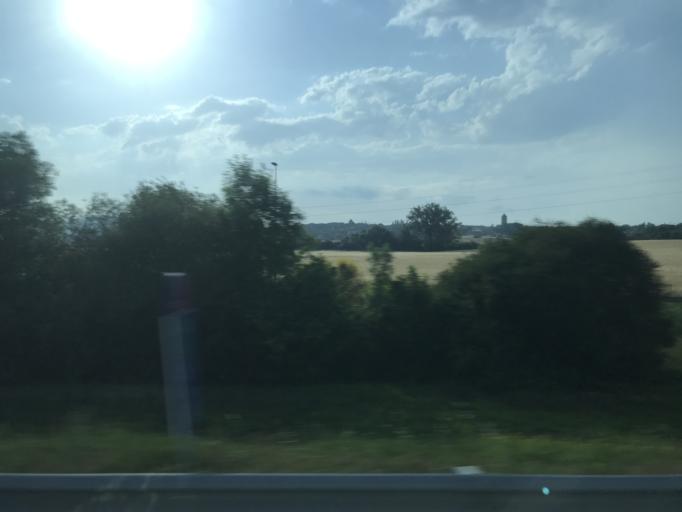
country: ES
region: Basque Country
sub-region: Provincia de Alava
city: Gasteiz / Vitoria
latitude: 42.9102
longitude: -2.7033
